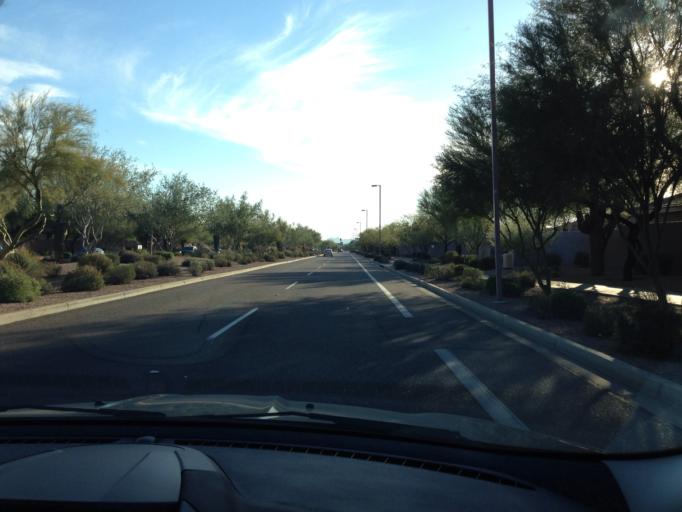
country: US
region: Arizona
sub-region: Maricopa County
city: Carefree
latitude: 33.6905
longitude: -111.9721
